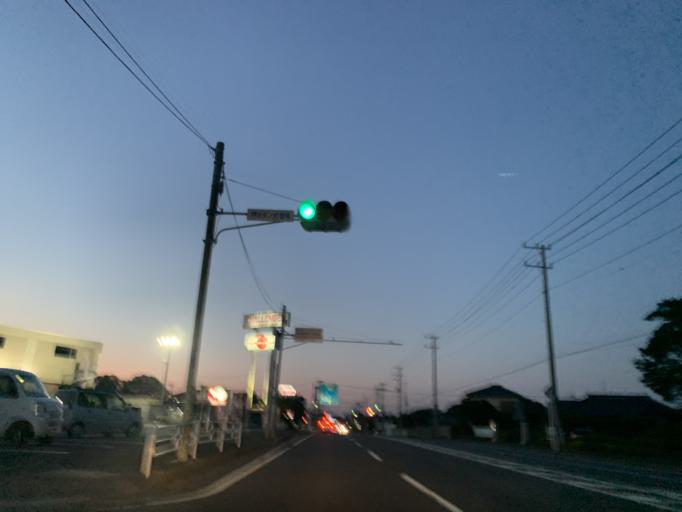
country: JP
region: Chiba
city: Nagareyama
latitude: 35.8765
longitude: 139.9061
